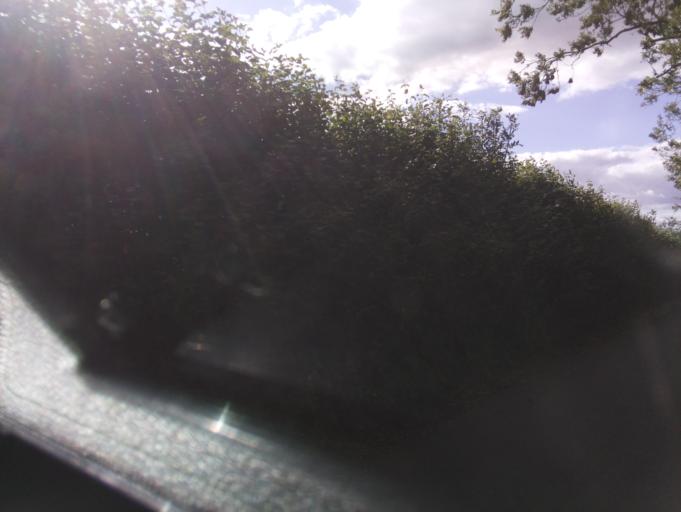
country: GB
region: England
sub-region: Hampshire
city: Chandlers Ford
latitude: 51.0544
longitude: -1.3811
